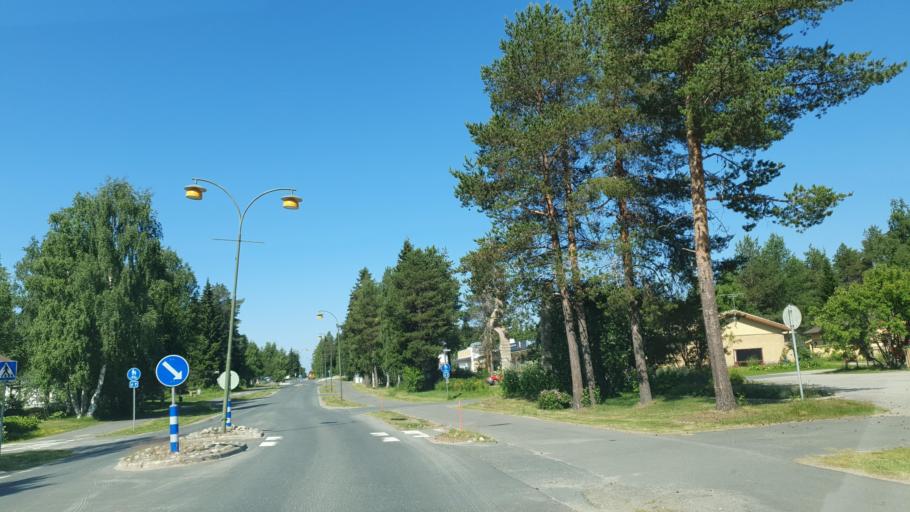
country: FI
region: Lapland
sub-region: Rovaniemi
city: Ranua
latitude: 65.9315
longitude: 26.5131
